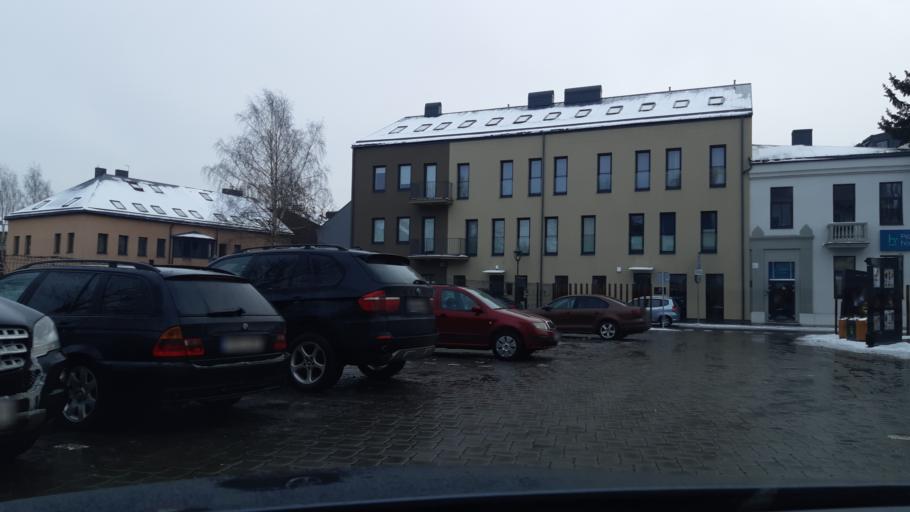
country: LT
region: Kauno apskritis
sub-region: Kaunas
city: Kaunas
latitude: 54.8947
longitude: 23.8979
